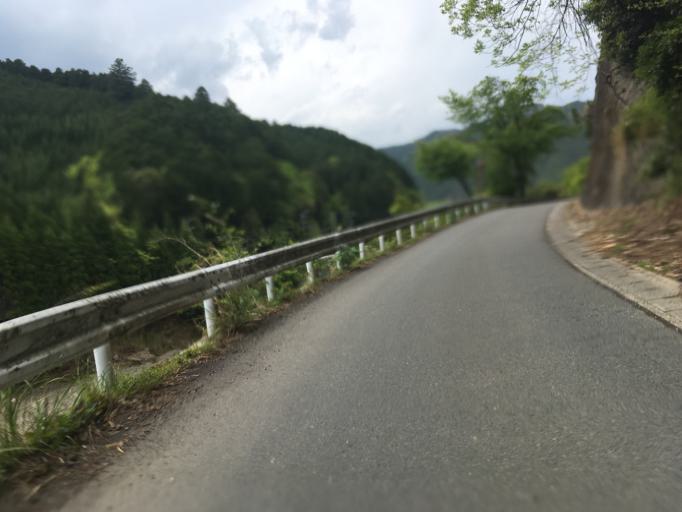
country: JP
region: Kyoto
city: Kameoka
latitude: 35.1406
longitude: 135.5756
